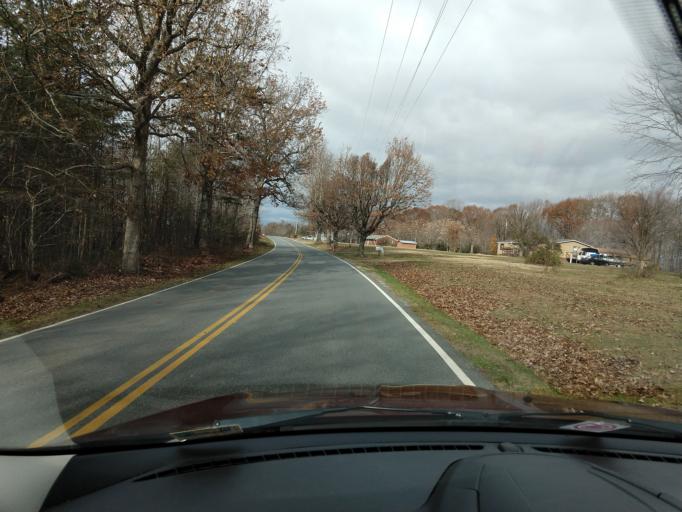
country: US
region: Virginia
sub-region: Franklin County
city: North Shore
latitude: 37.1736
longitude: -79.6381
